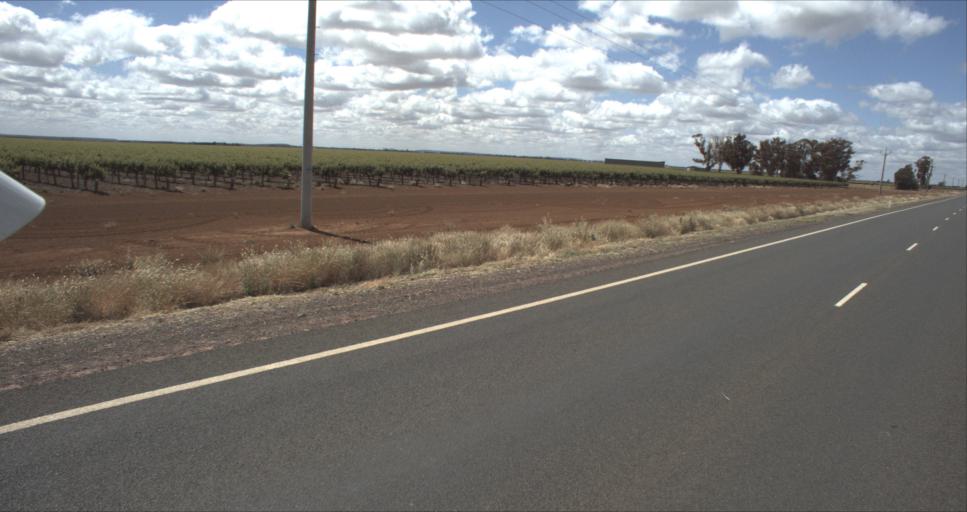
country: AU
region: New South Wales
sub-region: Murrumbidgee Shire
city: Darlington Point
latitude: -34.4718
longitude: 146.1418
